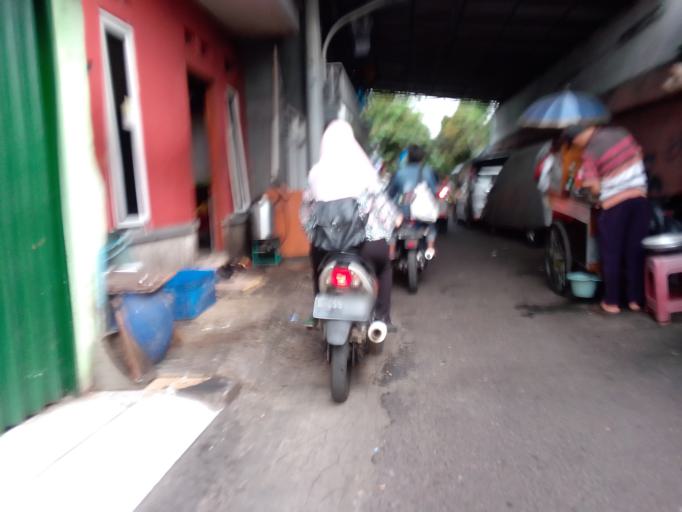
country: ID
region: Jakarta Raya
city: Jakarta
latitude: -6.1642
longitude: 106.7998
